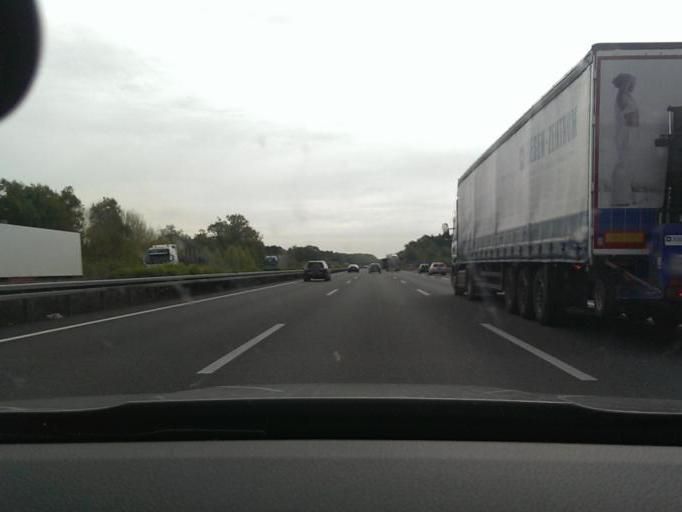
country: DE
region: Lower Saxony
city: Braunschweig
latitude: 52.3131
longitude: 10.5543
